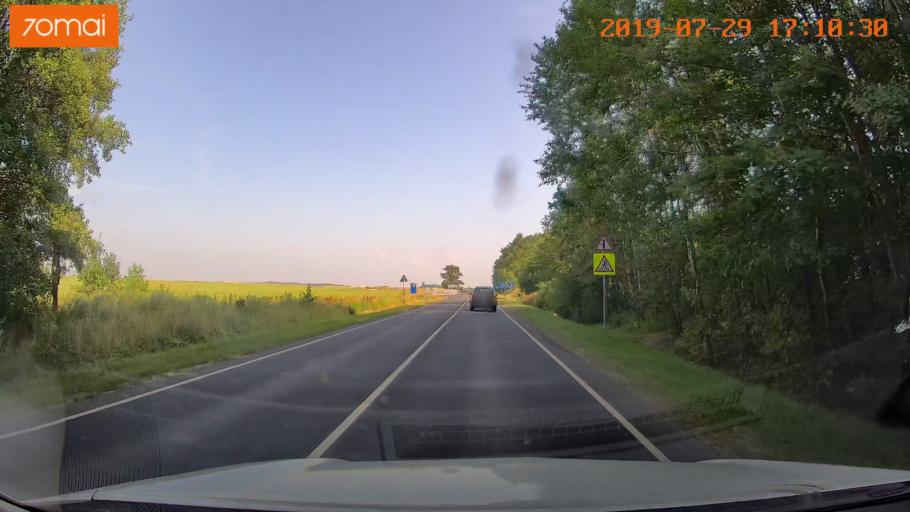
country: RU
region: Kaliningrad
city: Vzmorye
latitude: 54.8018
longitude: 20.3693
